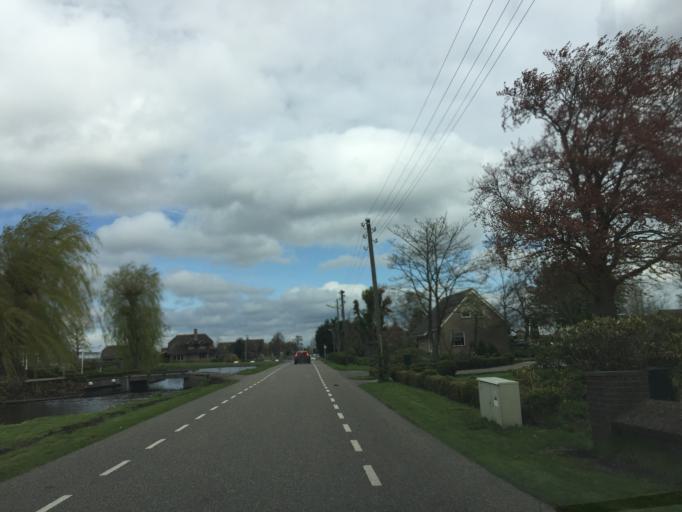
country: NL
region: South Holland
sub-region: Gemeente Waddinxveen
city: Vondelwijk
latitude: 52.0621
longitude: 4.6712
